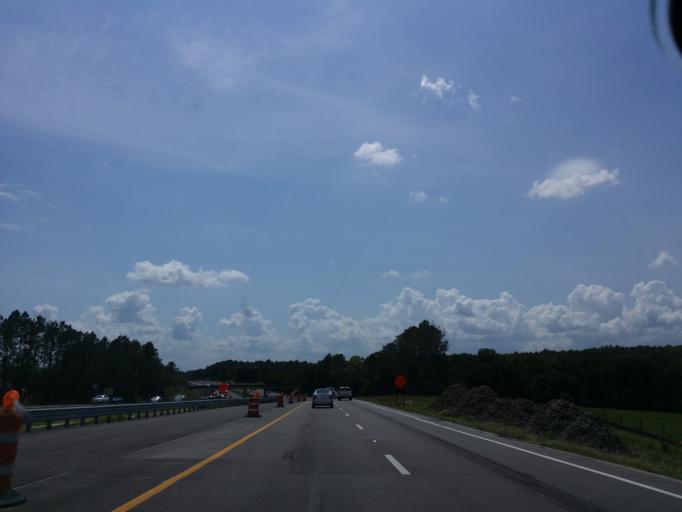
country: US
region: Florida
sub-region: Pasco County
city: San Antonio
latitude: 28.4221
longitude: -82.2868
